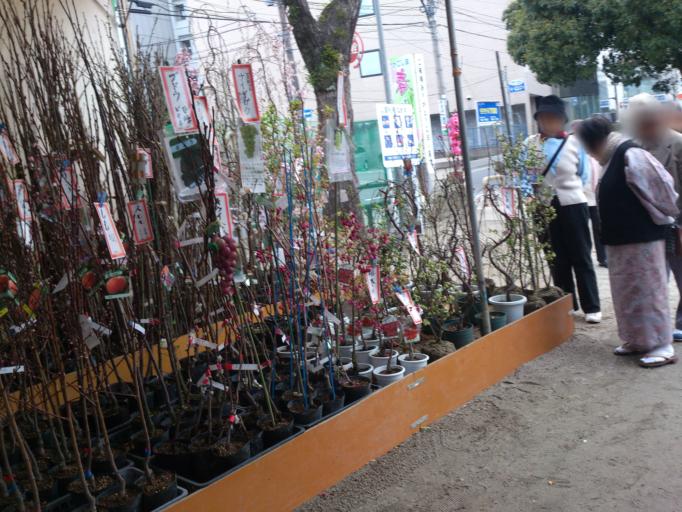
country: JP
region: Kagoshima
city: Kagoshima-shi
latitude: 31.5873
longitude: 130.5461
